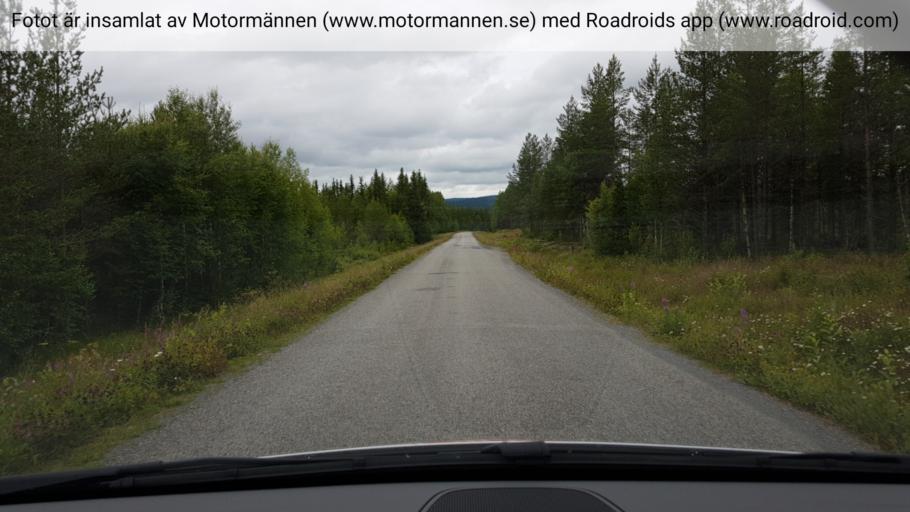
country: SE
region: Jaemtland
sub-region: Krokoms Kommun
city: Krokom
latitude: 63.7590
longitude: 14.3637
